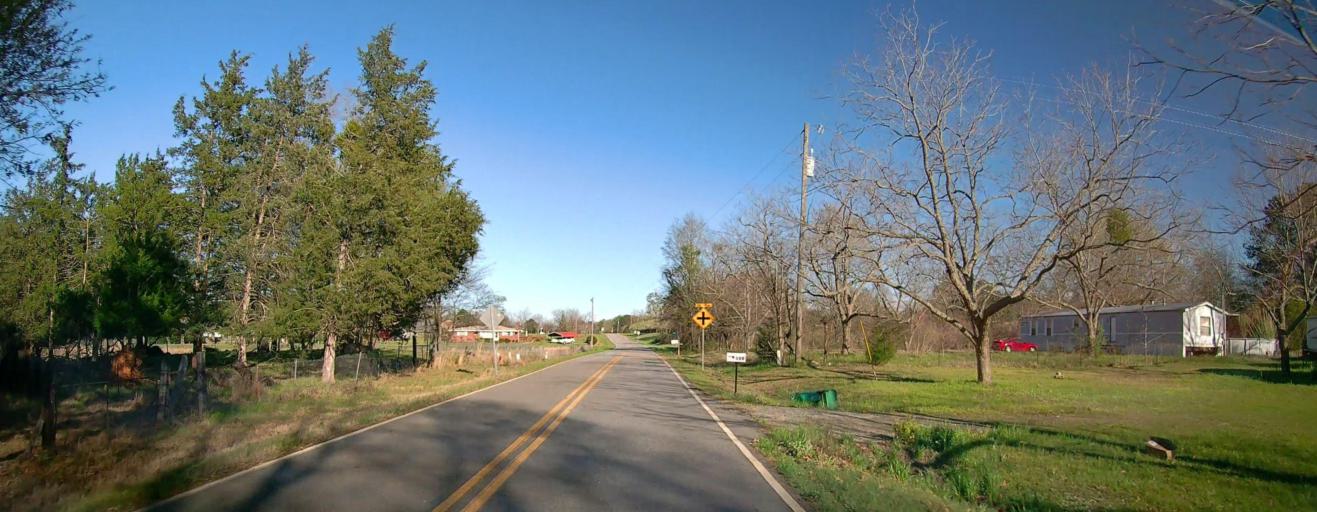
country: US
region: Georgia
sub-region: Houston County
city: Perry
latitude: 32.3640
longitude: -83.6646
